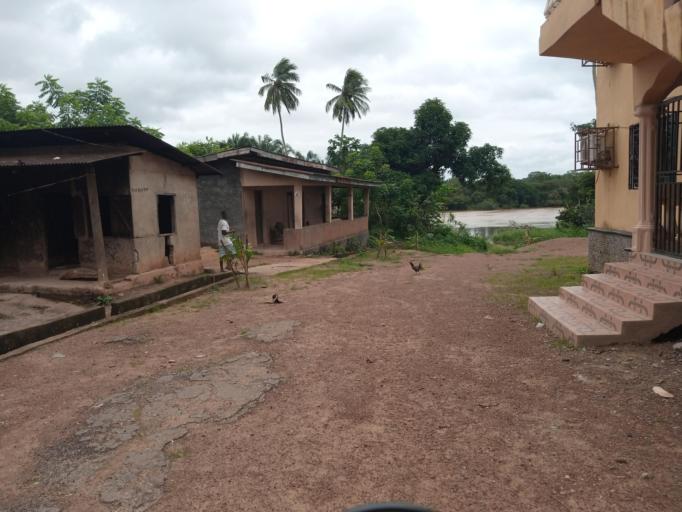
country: SL
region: Southern Province
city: Largo
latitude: 8.2053
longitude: -12.0626
